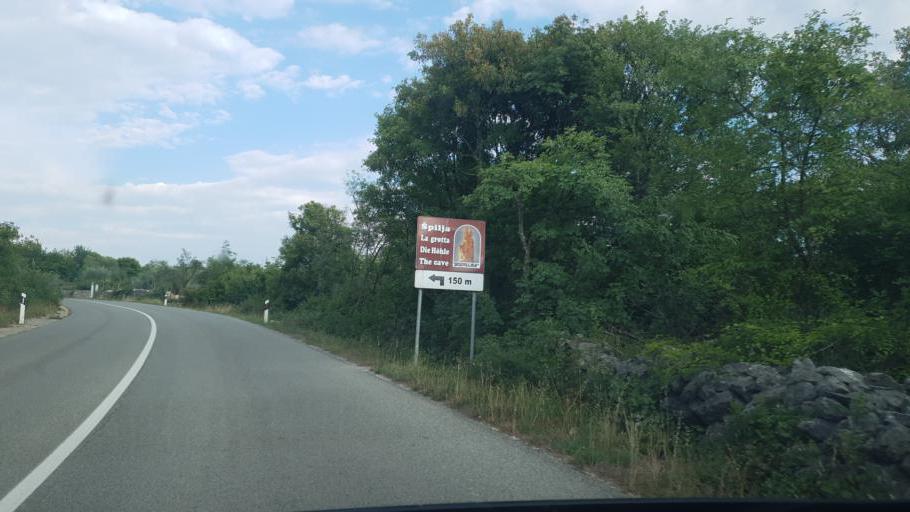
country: HR
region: Primorsko-Goranska
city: Njivice
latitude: 45.1212
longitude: 14.5529
